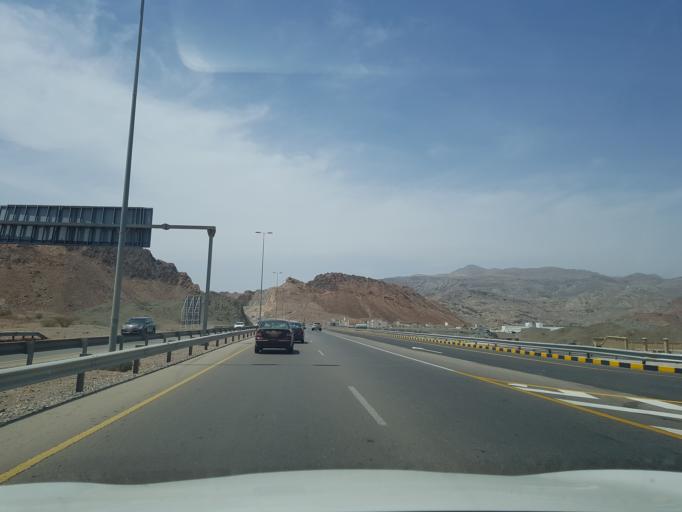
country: OM
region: Muhafazat ad Dakhiliyah
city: Bidbid
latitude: 23.4634
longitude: 58.1222
